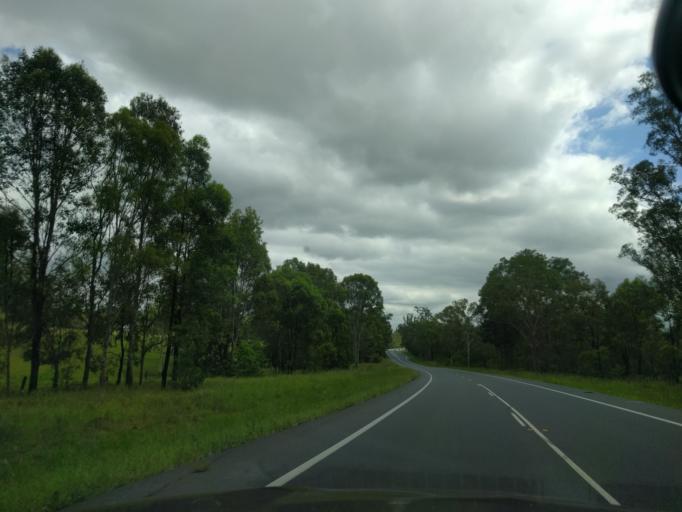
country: AU
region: Queensland
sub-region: Logan
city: Cedar Vale
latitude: -27.8693
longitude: 152.9987
